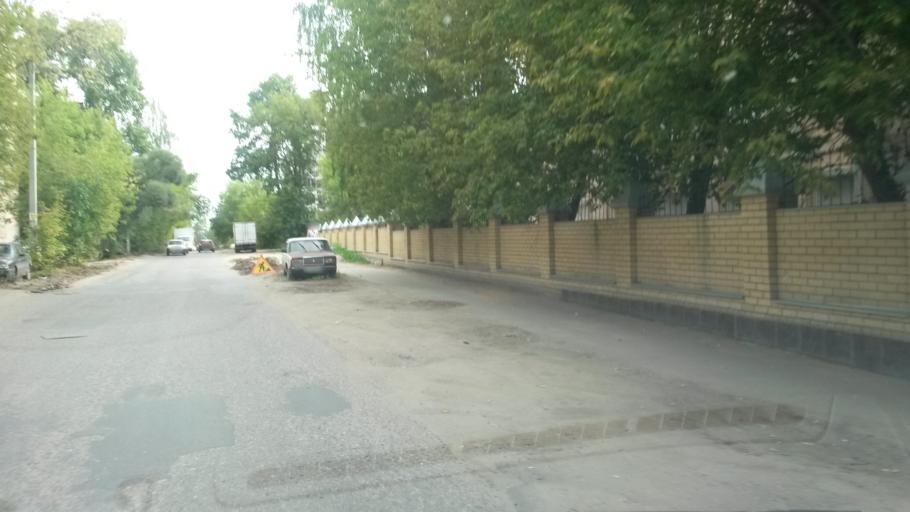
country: RU
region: Ivanovo
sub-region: Gorod Ivanovo
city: Ivanovo
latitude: 57.0042
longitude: 40.9566
